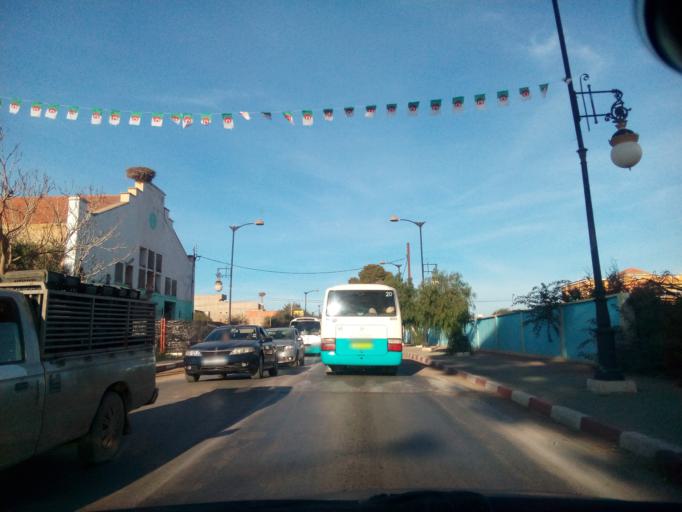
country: DZ
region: Mostaganem
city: Mostaganem
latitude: 35.7781
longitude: 0.1924
